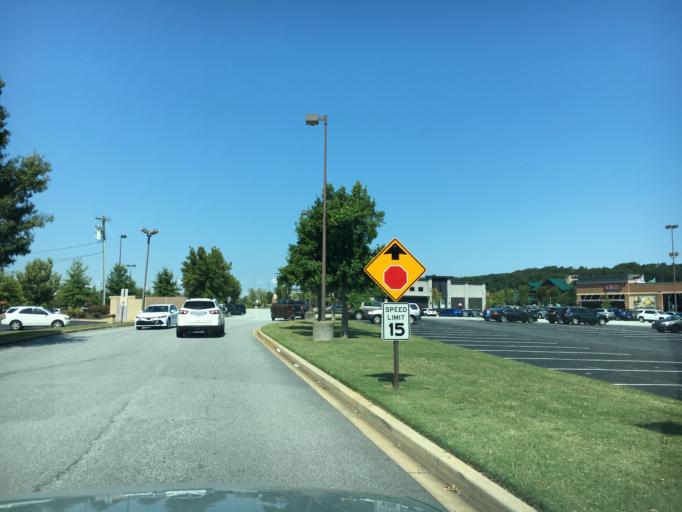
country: US
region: South Carolina
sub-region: Greenville County
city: Mauldin
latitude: 34.8319
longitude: -82.3057
